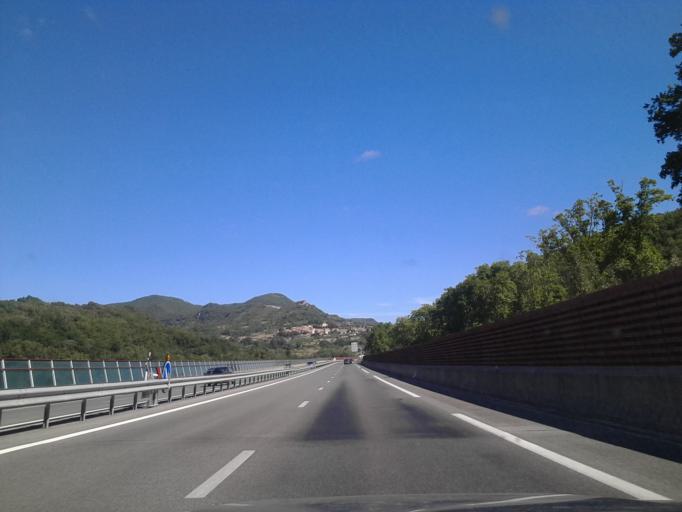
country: FR
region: Languedoc-Roussillon
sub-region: Departement de l'Herault
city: Lodeve
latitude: 43.7494
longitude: 3.3304
